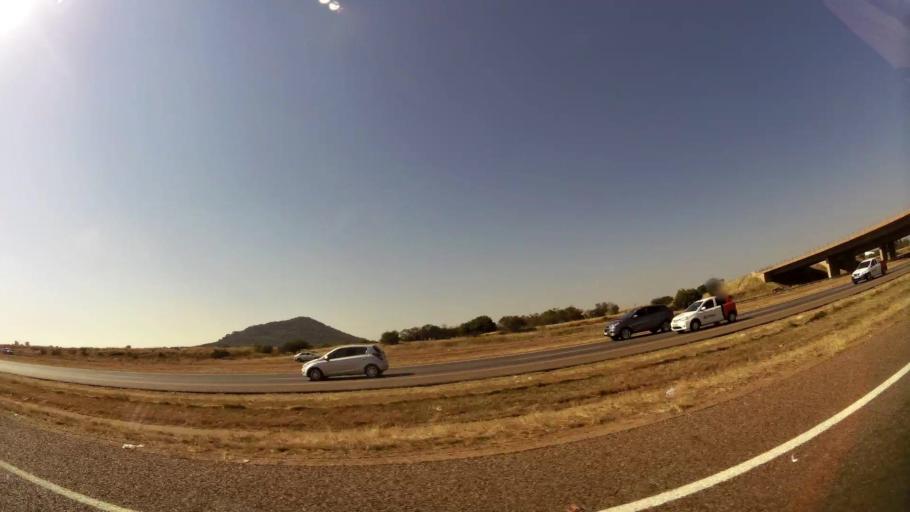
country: ZA
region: North-West
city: Ga-Rankuwa
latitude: -25.6281
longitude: 28.1106
